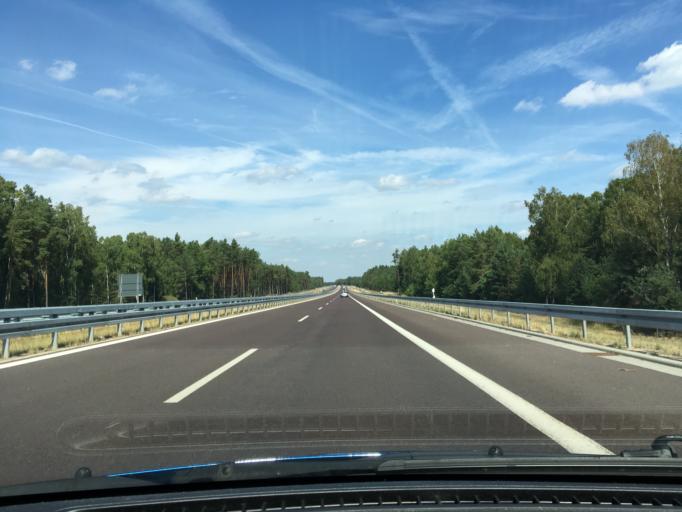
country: DE
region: Mecklenburg-Vorpommern
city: Ludwigslust
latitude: 53.3089
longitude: 11.5278
